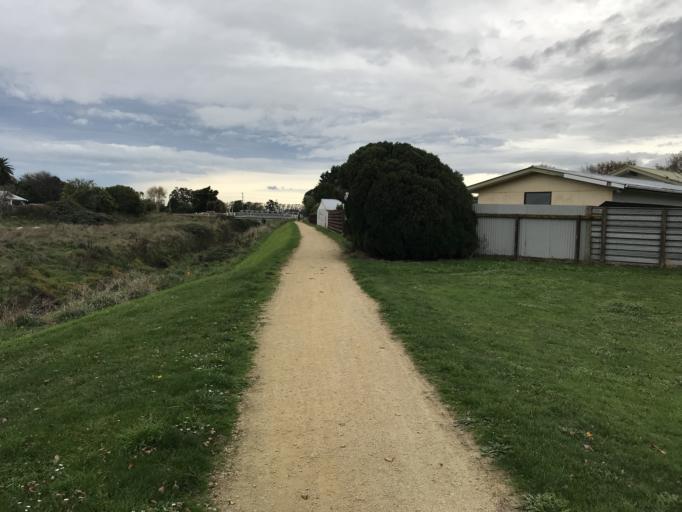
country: NZ
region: Manawatu-Wanganui
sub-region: Palmerston North City
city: Palmerston North
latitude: -40.3742
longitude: 175.5753
